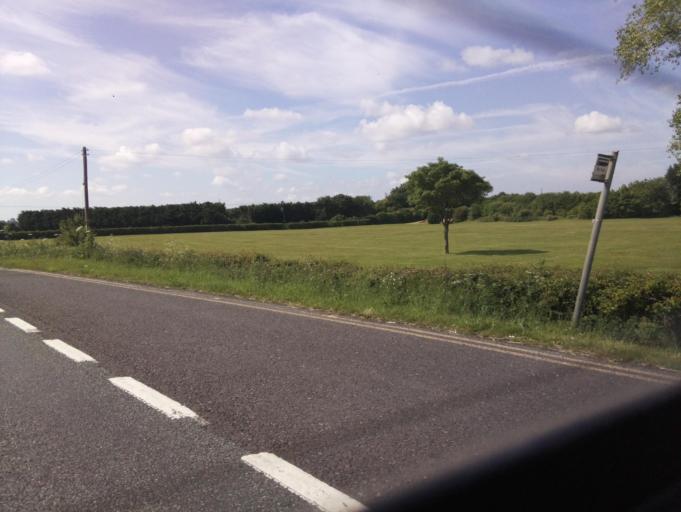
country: GB
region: England
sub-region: Lincolnshire
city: Burton
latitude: 53.2853
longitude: -0.5405
